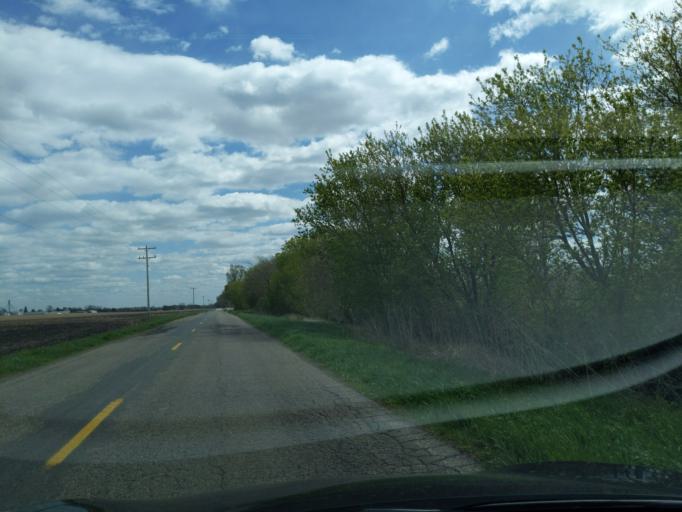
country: US
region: Michigan
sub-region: Ingham County
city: Mason
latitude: 42.5344
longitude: -84.5422
